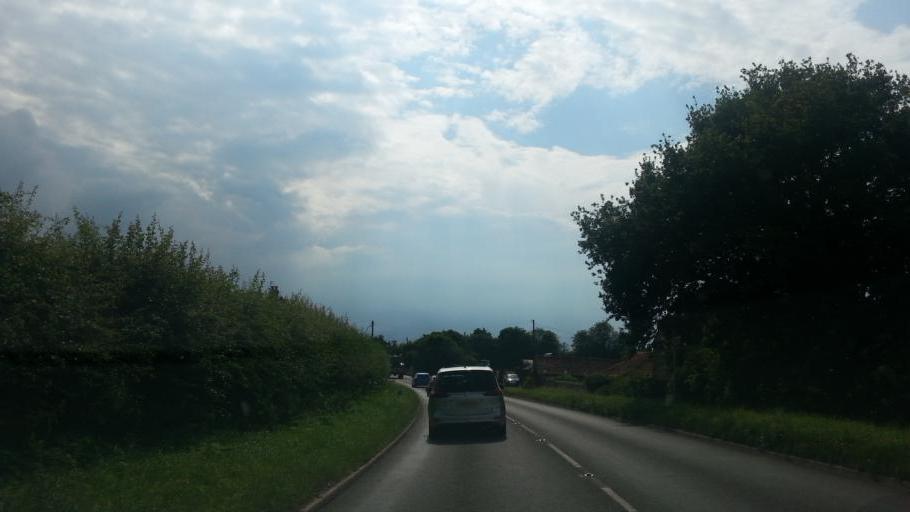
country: GB
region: England
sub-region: Norfolk
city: Sheringham
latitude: 52.9181
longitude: 1.1639
